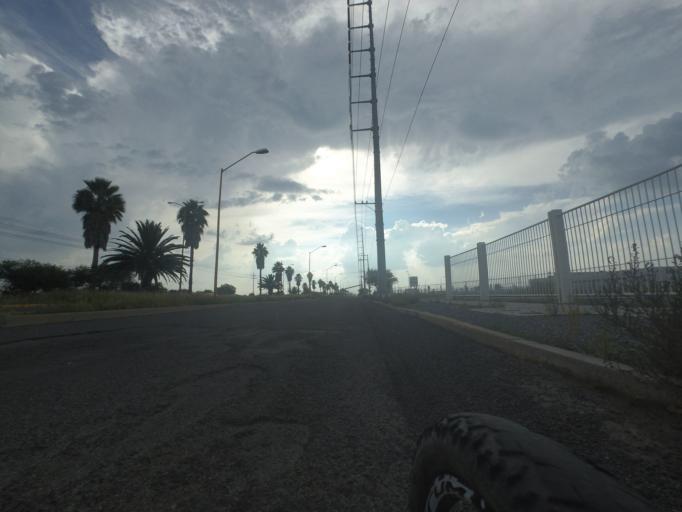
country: MX
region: Aguascalientes
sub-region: Aguascalientes
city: Penuelas (El Cienegal)
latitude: 21.7252
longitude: -102.2961
